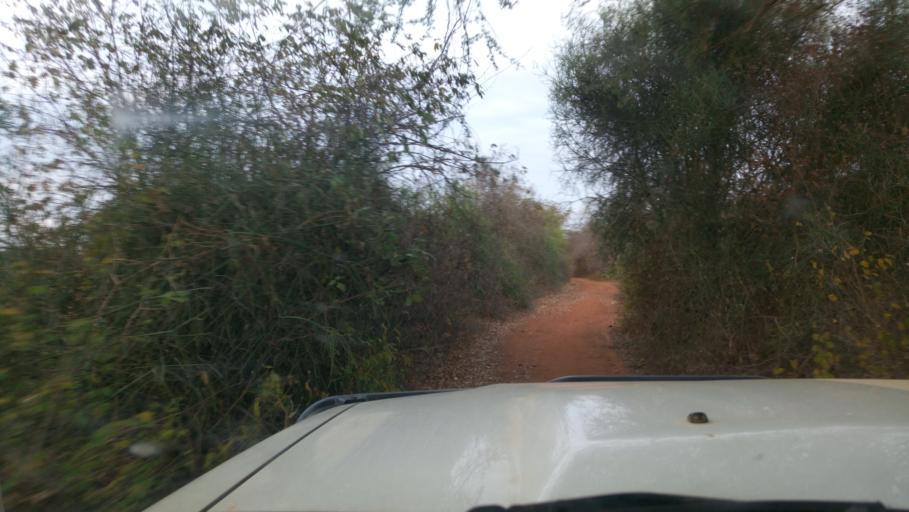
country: KE
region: Kitui
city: Kitui
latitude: -1.8858
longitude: 38.2318
